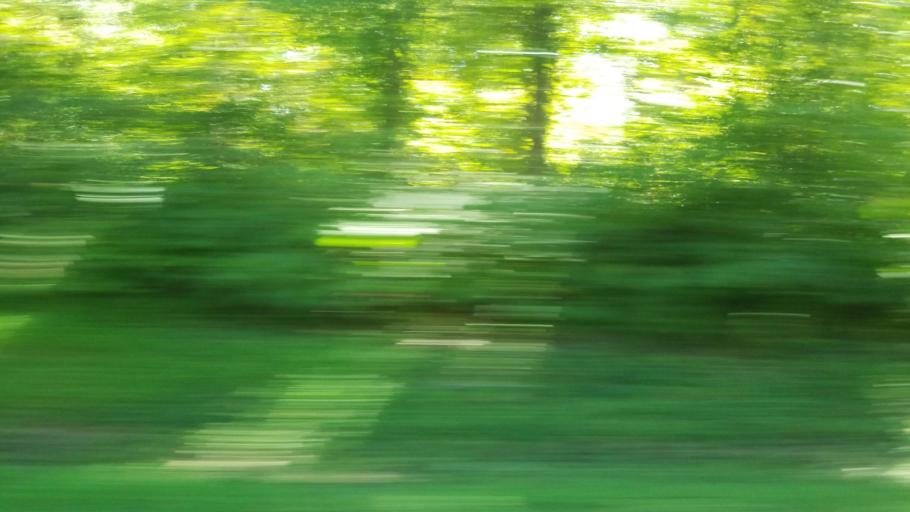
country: US
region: Illinois
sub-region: Williamson County
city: Johnston City
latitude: 37.7893
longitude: -88.9002
